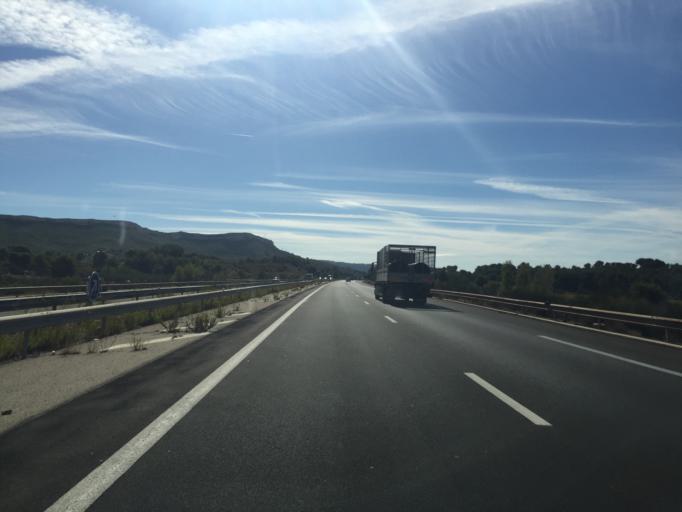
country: FR
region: Provence-Alpes-Cote d'Azur
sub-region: Departement des Bouches-du-Rhone
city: Rognac
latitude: 43.5051
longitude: 5.2371
